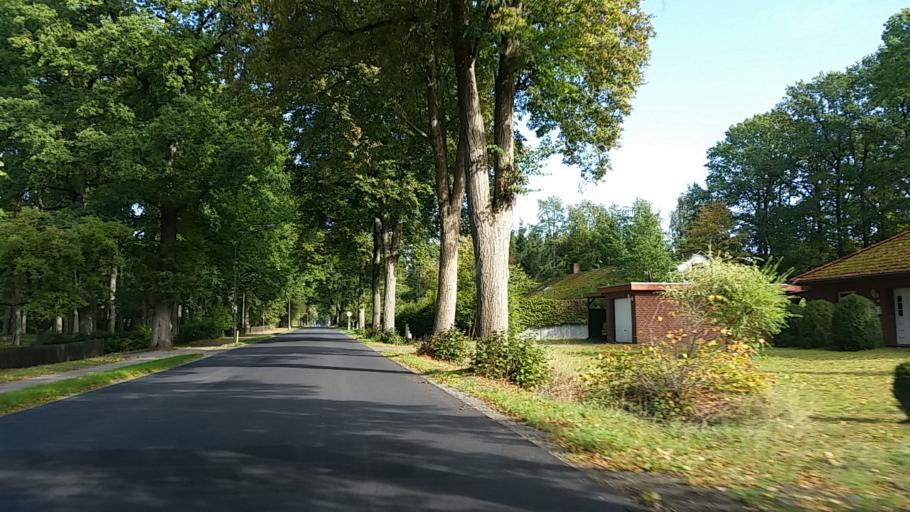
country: DE
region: Lower Saxony
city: Neuenkirchen
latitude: 53.0148
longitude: 9.6531
